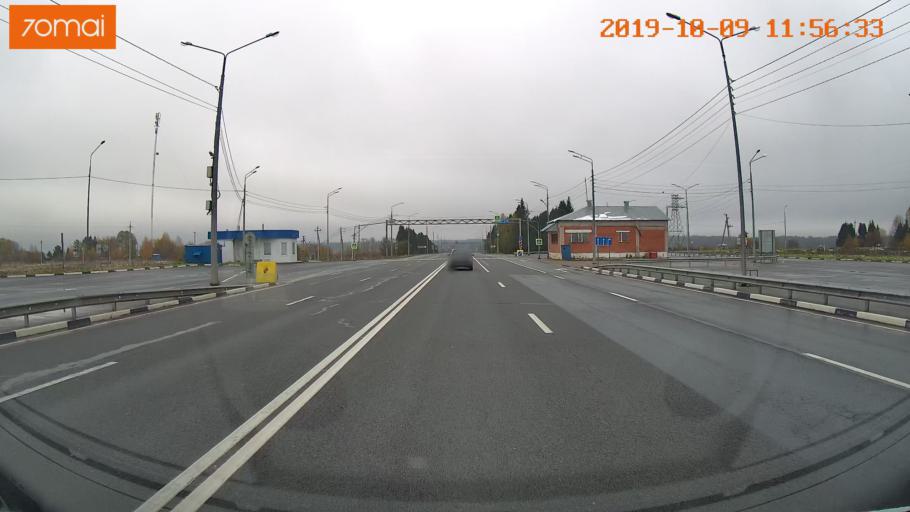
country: RU
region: Vologda
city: Gryazovets
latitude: 58.7428
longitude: 40.2882
